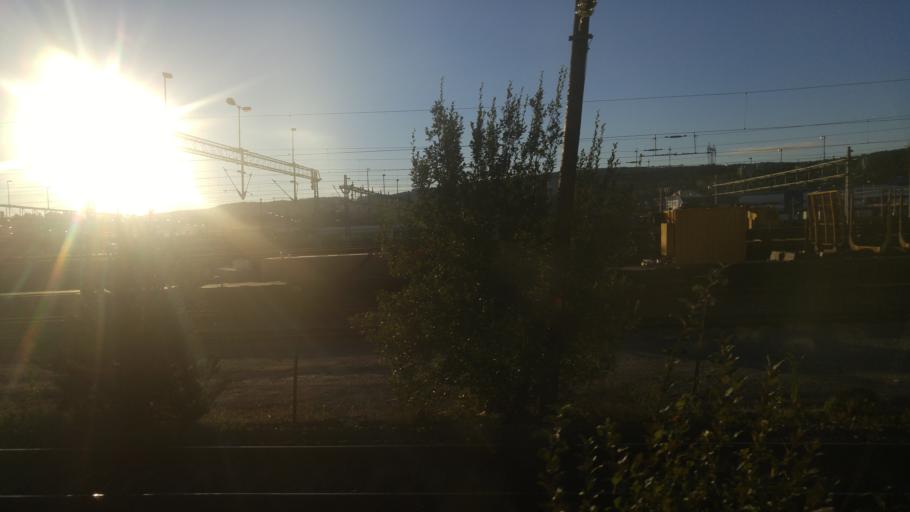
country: NO
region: Oslo
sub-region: Oslo
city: Oslo
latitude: 59.9309
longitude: 10.8344
